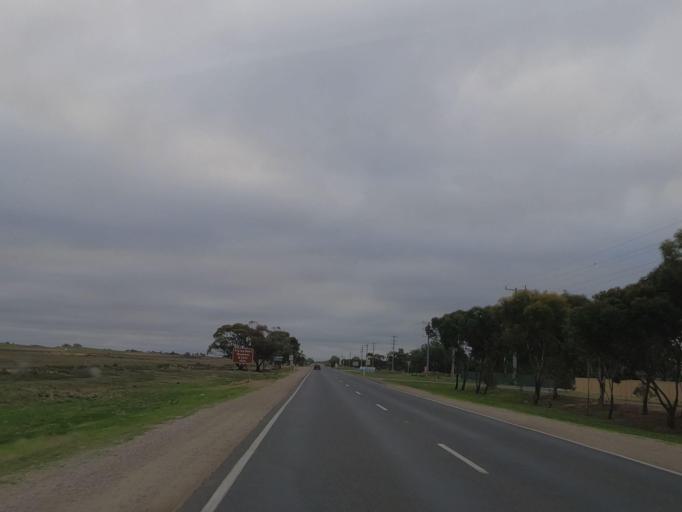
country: AU
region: Victoria
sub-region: Swan Hill
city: Swan Hill
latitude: -35.4530
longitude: 143.6264
